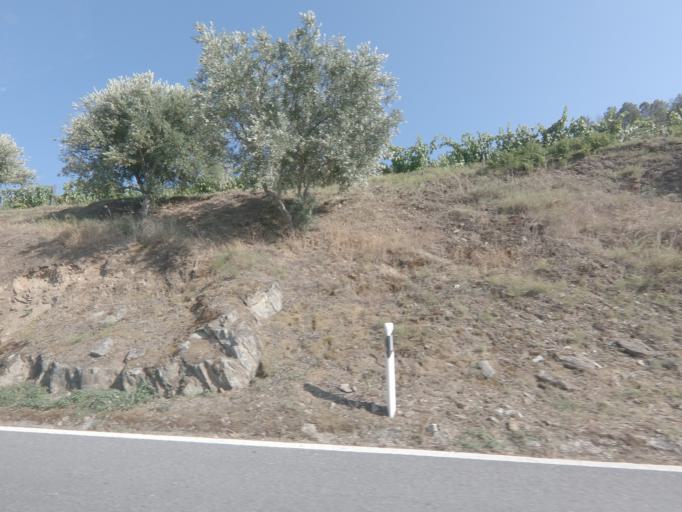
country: PT
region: Viseu
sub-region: Tabuaco
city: Tabuaco
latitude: 41.1403
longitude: -7.5659
